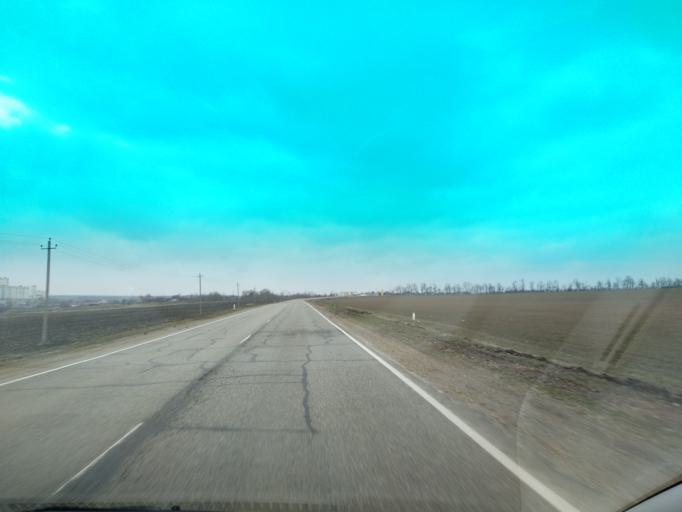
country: RU
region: Krasnodarskiy
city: Novomalorossiyskaya
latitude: 45.7116
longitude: 39.8677
